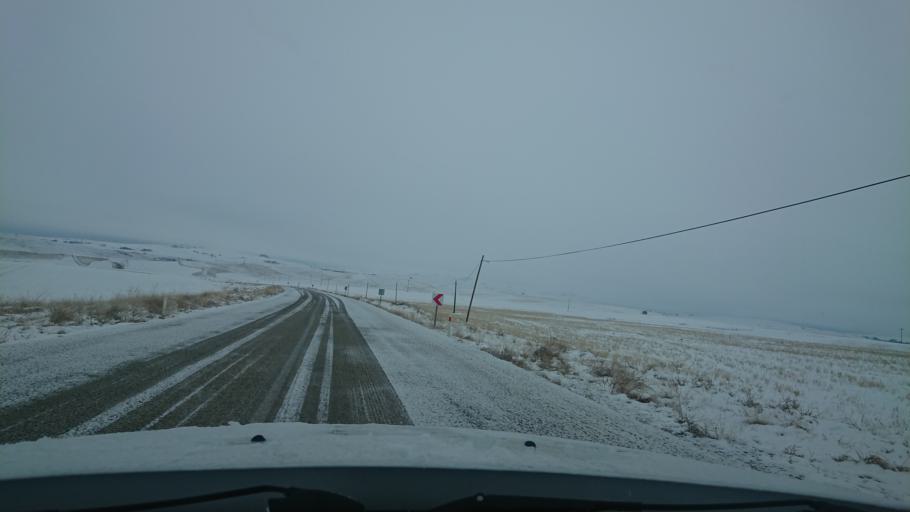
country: TR
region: Aksaray
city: Agacoren
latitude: 38.7791
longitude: 33.8713
